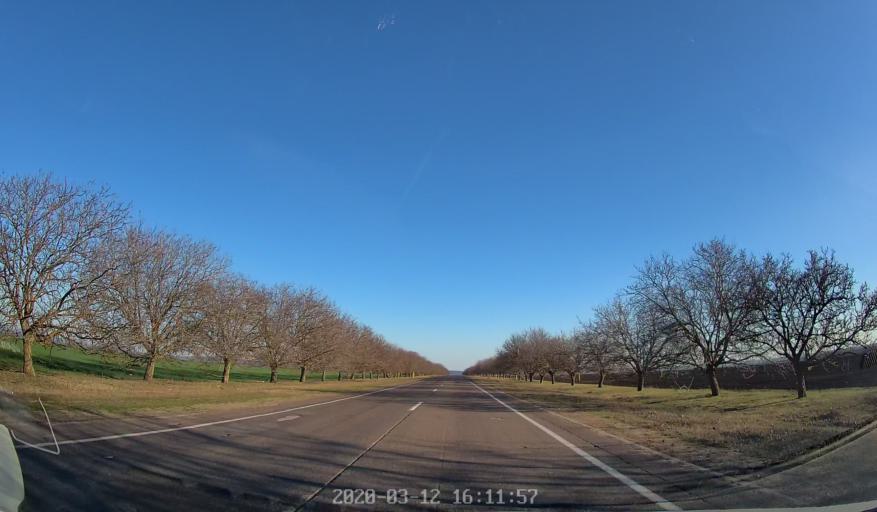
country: MD
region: Anenii Noi
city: Anenii Noi
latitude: 46.9417
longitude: 29.2662
